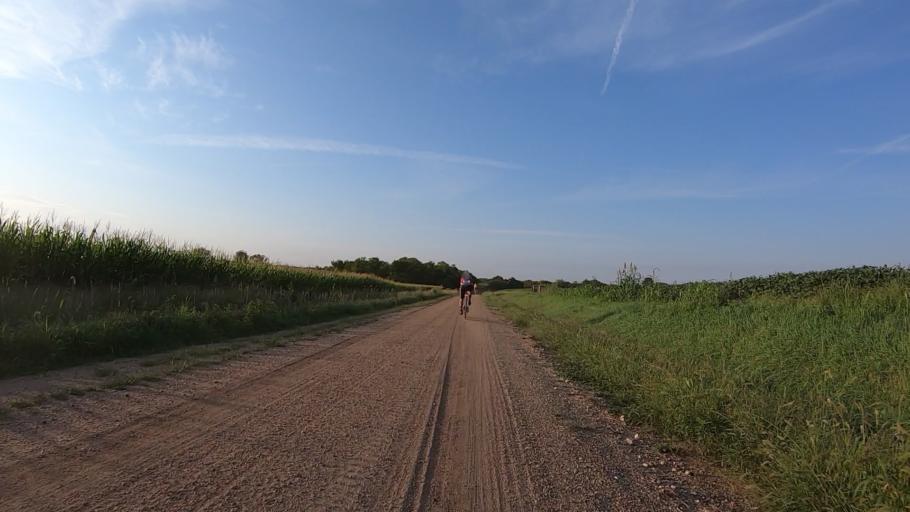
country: US
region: Kansas
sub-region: Marshall County
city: Blue Rapids
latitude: 39.7637
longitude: -96.7508
